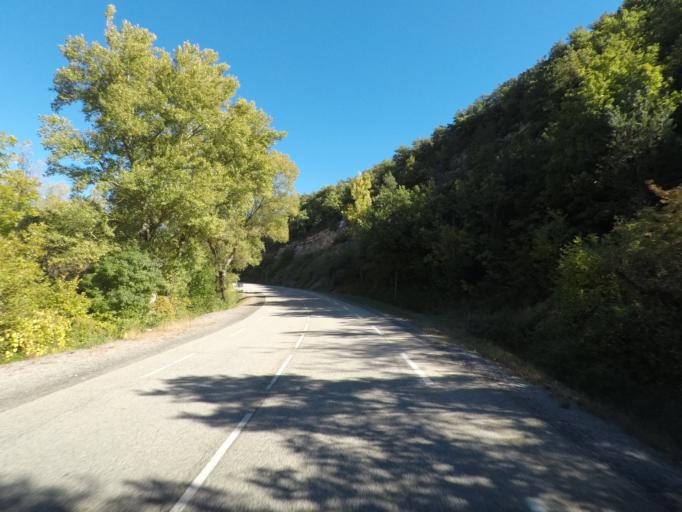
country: FR
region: Rhone-Alpes
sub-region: Departement de la Drome
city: Buis-les-Baronnies
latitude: 44.3796
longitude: 5.4205
